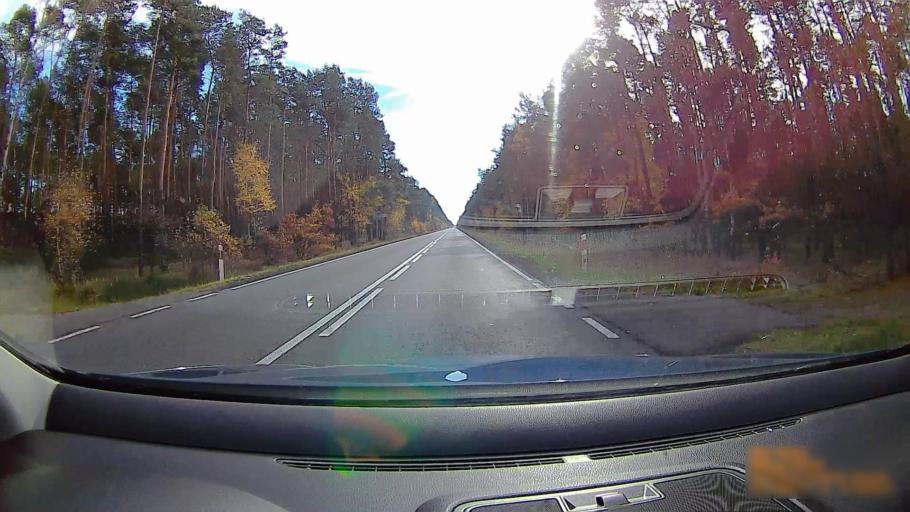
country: PL
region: Greater Poland Voivodeship
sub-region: Powiat ostrzeszowski
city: Ostrzeszow
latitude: 51.4781
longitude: 17.8872
